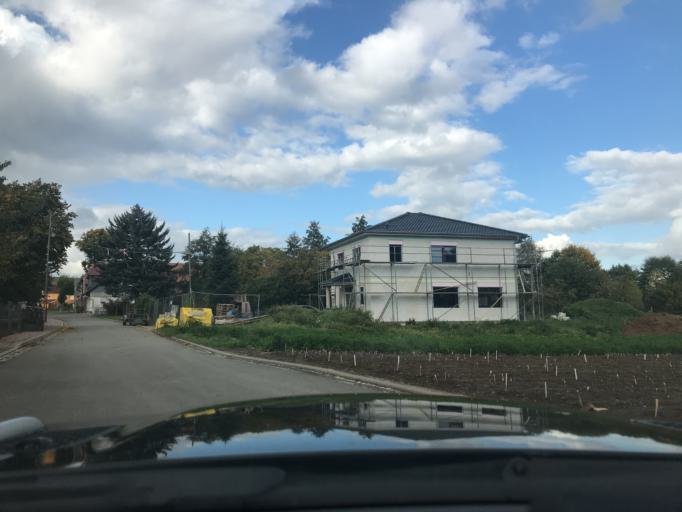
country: DE
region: Thuringia
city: Flarchheim
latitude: 51.1263
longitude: 10.4836
